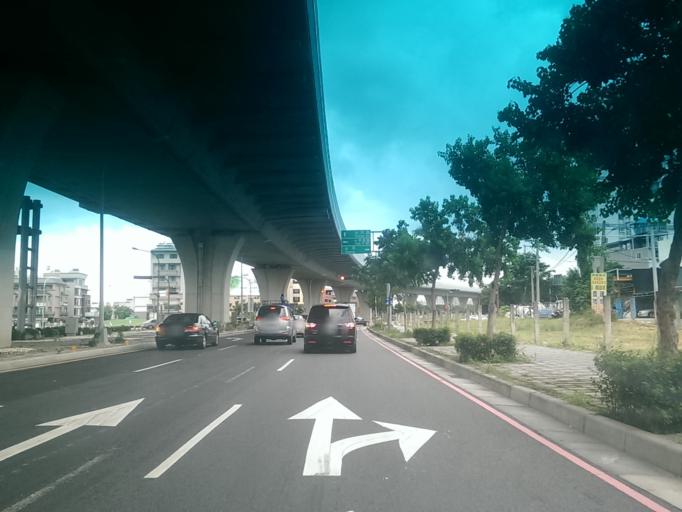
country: TW
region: Taiwan
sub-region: Taichung City
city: Taichung
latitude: 24.1400
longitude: 120.7106
